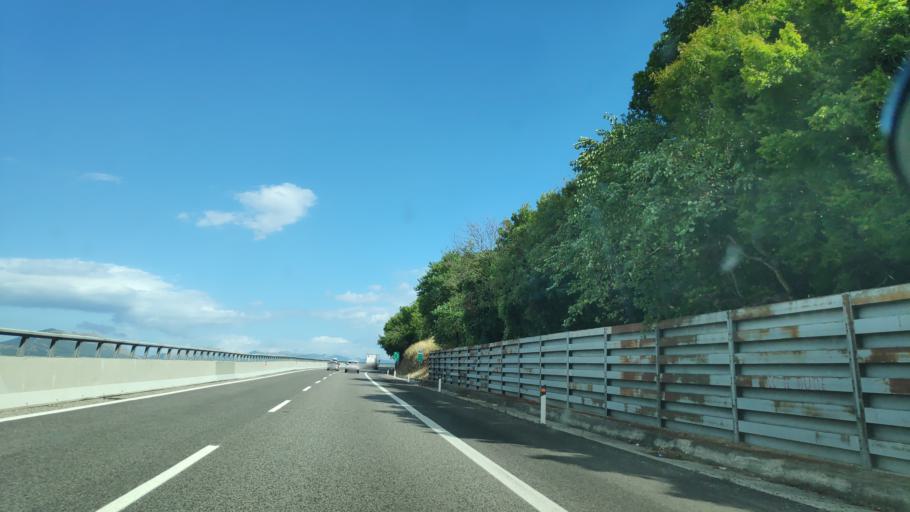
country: IT
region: Campania
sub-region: Provincia di Salerno
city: Sicignano degli Alburni
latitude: 40.5909
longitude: 15.3295
